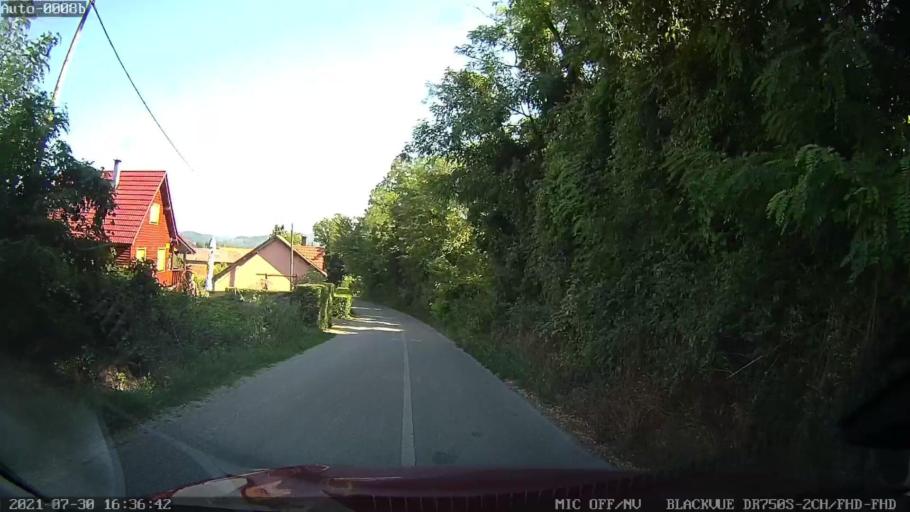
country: HR
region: Varazdinska
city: Jalzabet
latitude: 46.2390
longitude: 16.4740
